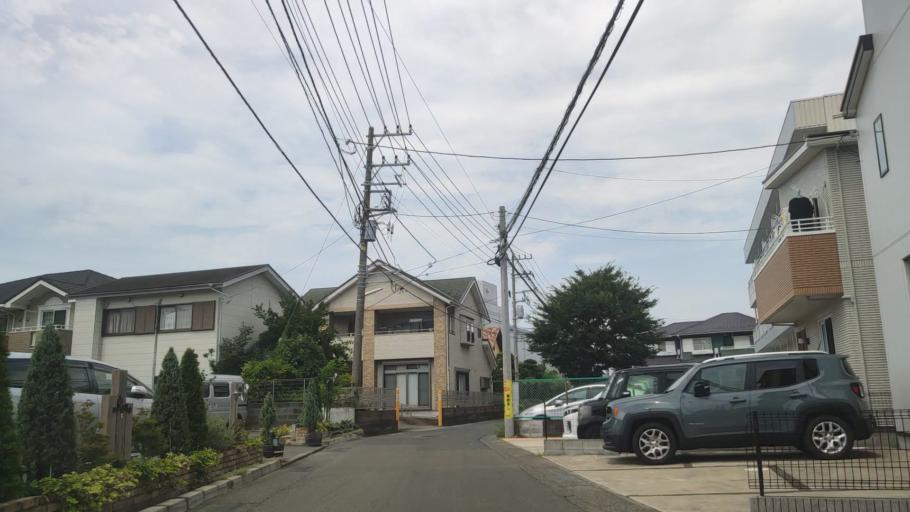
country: JP
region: Kanagawa
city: Atsugi
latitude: 35.4235
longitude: 139.3965
